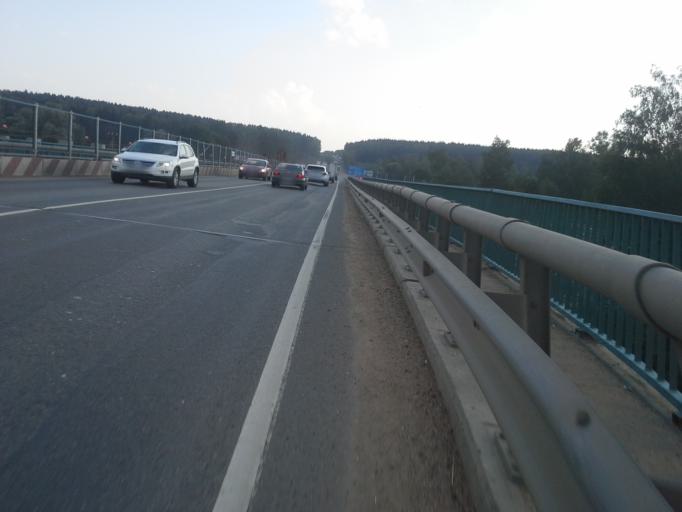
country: RU
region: Moskovskaya
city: Istra
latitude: 55.8585
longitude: 36.9354
